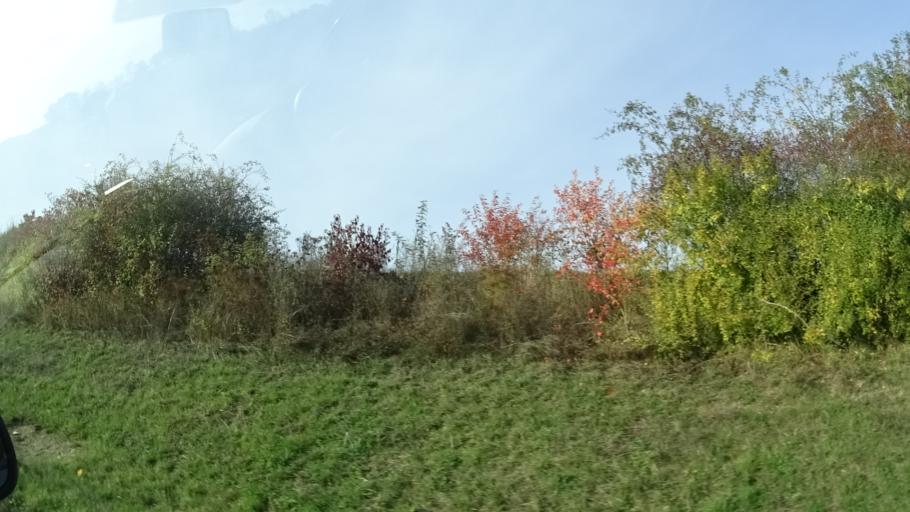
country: DE
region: Baden-Wuerttemberg
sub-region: Regierungsbezirk Stuttgart
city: Bad Mergentheim
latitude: 49.4503
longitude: 9.7462
